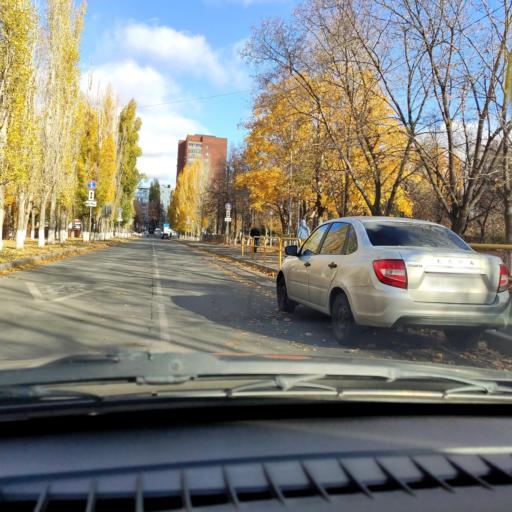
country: RU
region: Samara
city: Tol'yatti
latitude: 53.5228
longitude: 49.2855
